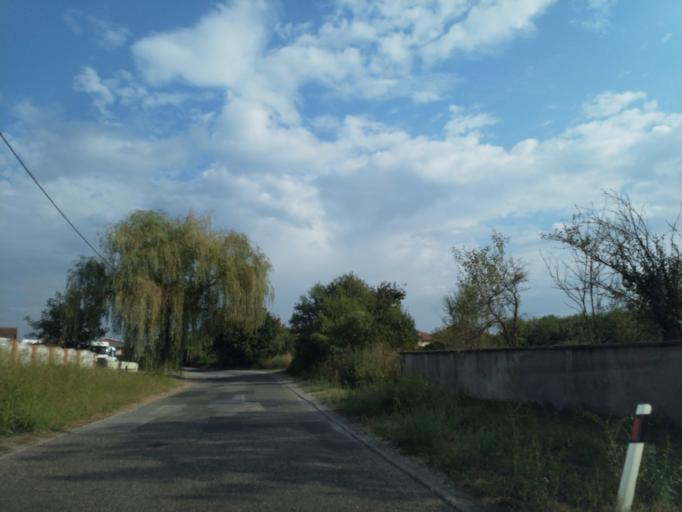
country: RS
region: Central Serbia
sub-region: Pomoravski Okrug
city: Paracin
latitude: 43.8541
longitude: 21.4418
